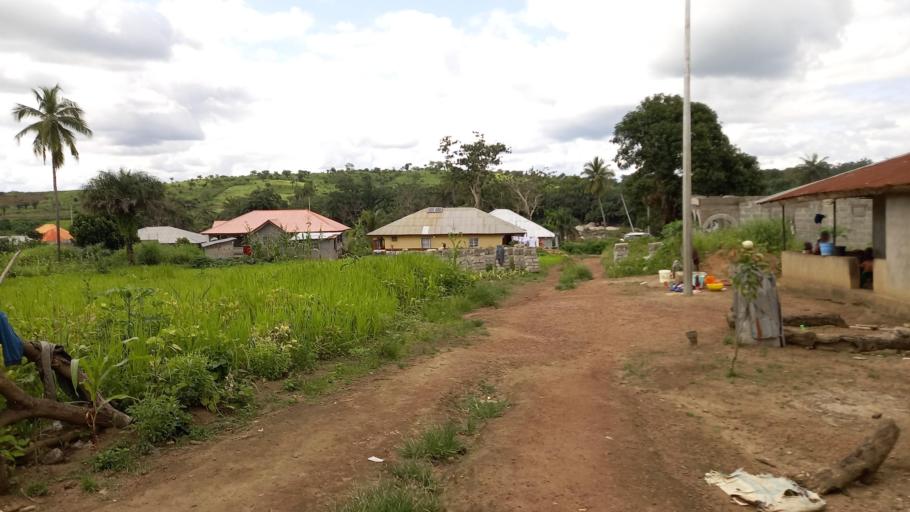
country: SL
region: Northern Province
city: Kamakwie
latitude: 9.5058
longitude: -12.2424
